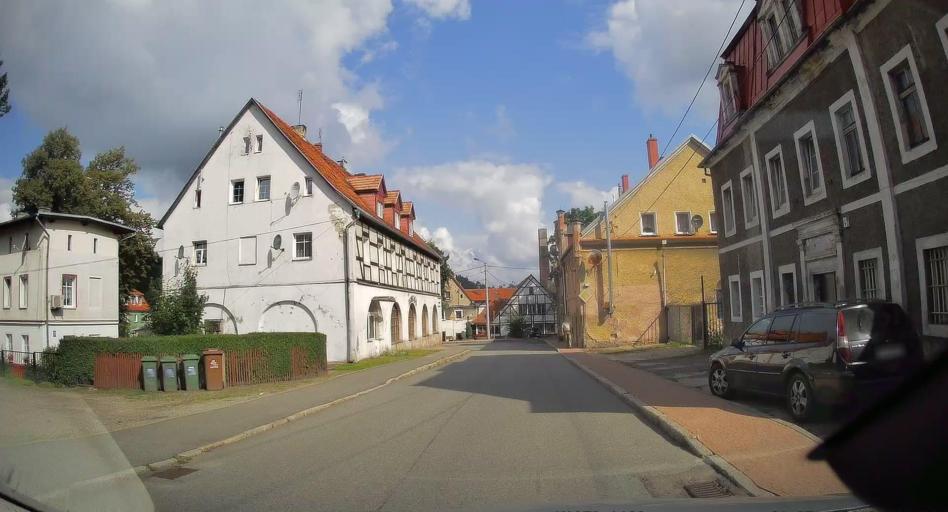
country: PL
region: Lower Silesian Voivodeship
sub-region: Powiat walbrzyski
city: Walim
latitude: 50.6994
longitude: 16.4410
